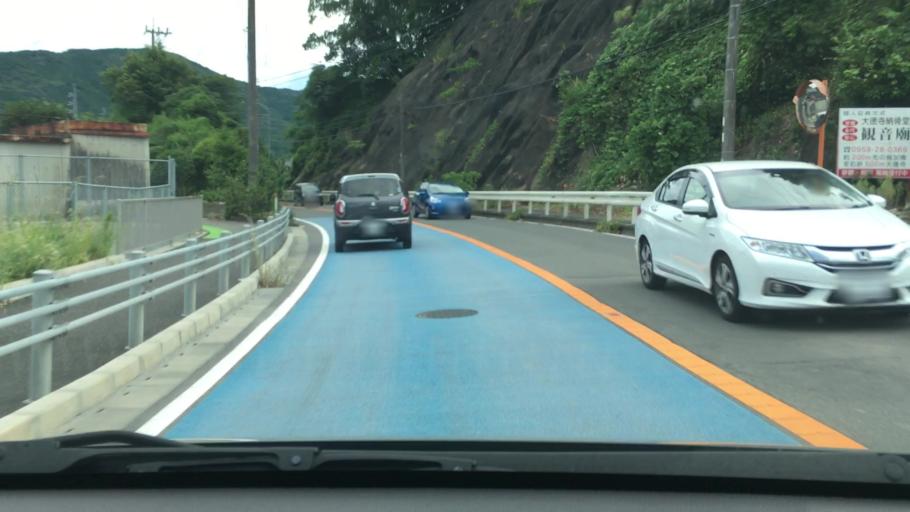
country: JP
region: Nagasaki
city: Sasebo
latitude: 32.9897
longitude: 129.7376
